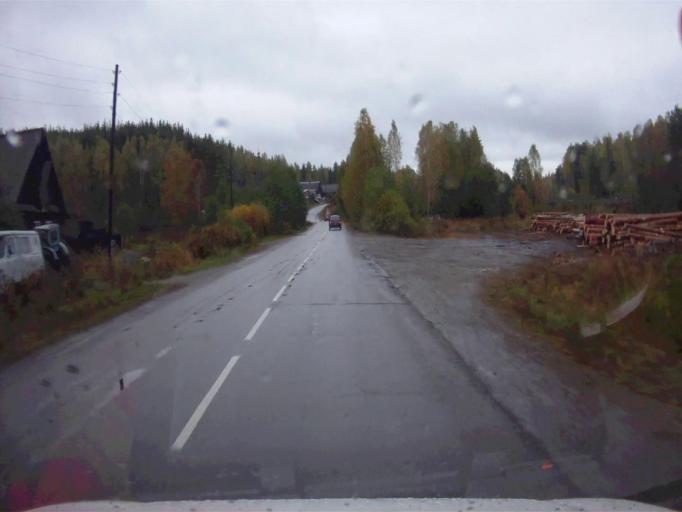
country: RU
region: Chelyabinsk
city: Kyshtym
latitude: 55.7633
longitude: 60.4859
